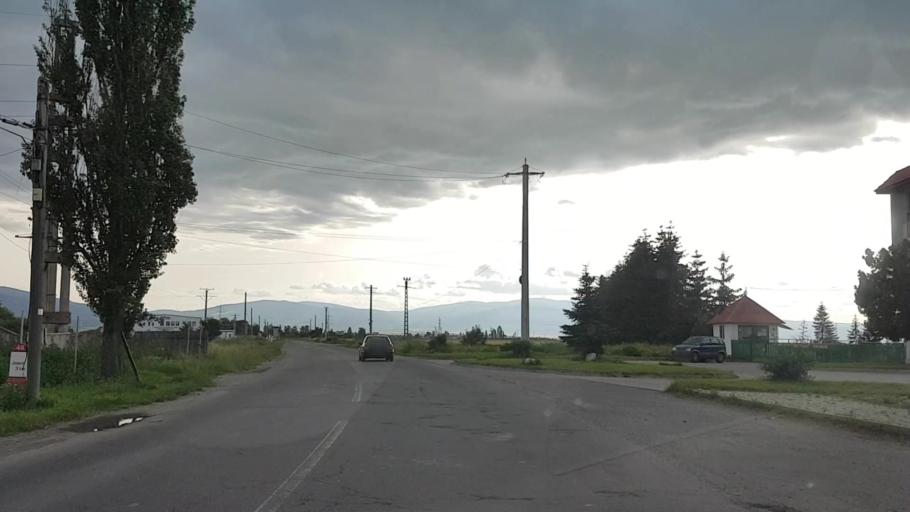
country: RO
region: Harghita
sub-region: Municipiul Gheorgheni
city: Gheorgheni
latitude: 46.7131
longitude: 25.5627
